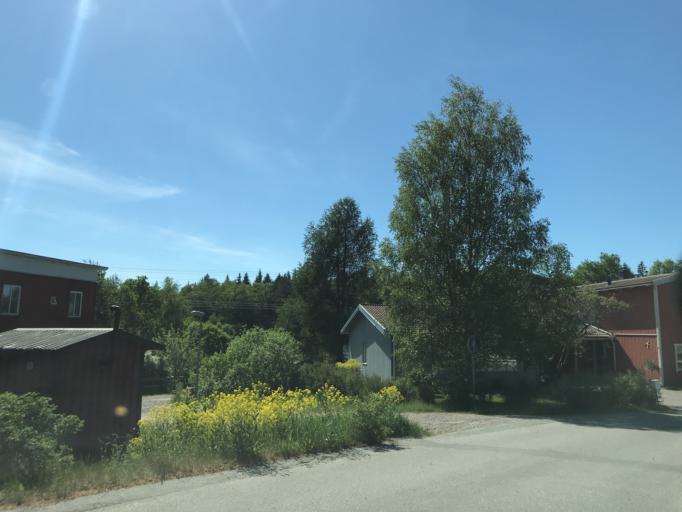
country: SE
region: Stockholm
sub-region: Jarfalla Kommun
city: Jakobsberg
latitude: 59.4522
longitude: 17.8907
